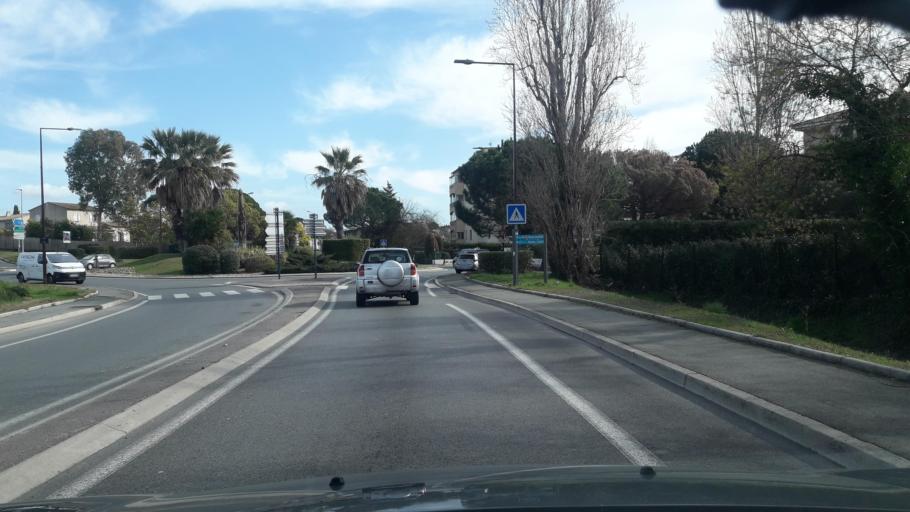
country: FR
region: Provence-Alpes-Cote d'Azur
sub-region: Departement du Var
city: Saint-Raphael
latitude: 43.4366
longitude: 6.7656
